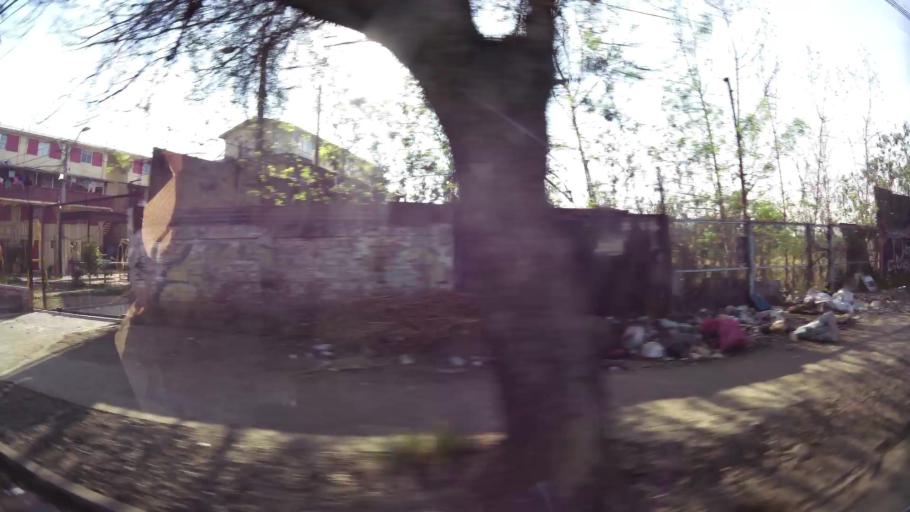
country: CL
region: Santiago Metropolitan
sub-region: Provincia de Santiago
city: Lo Prado
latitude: -33.4157
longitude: -70.7421
